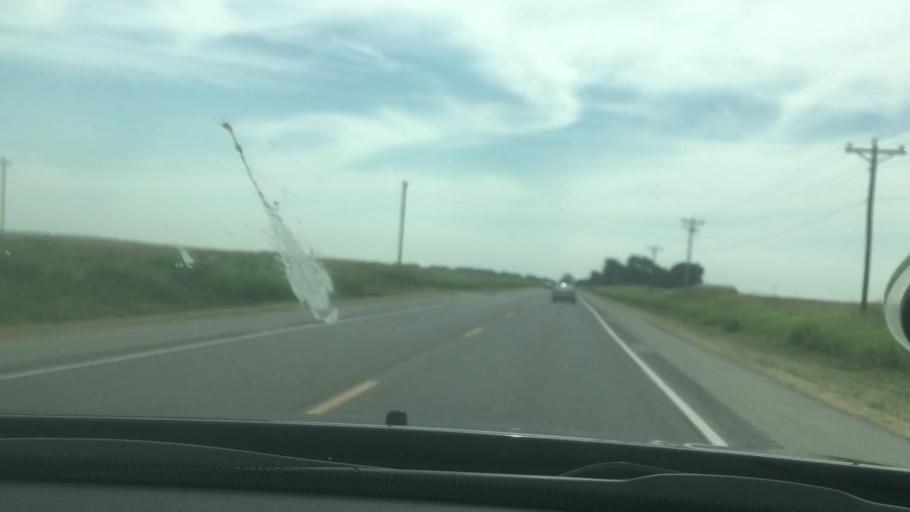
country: US
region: Oklahoma
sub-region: Garvin County
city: Lindsay
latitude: 34.8263
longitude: -97.5512
